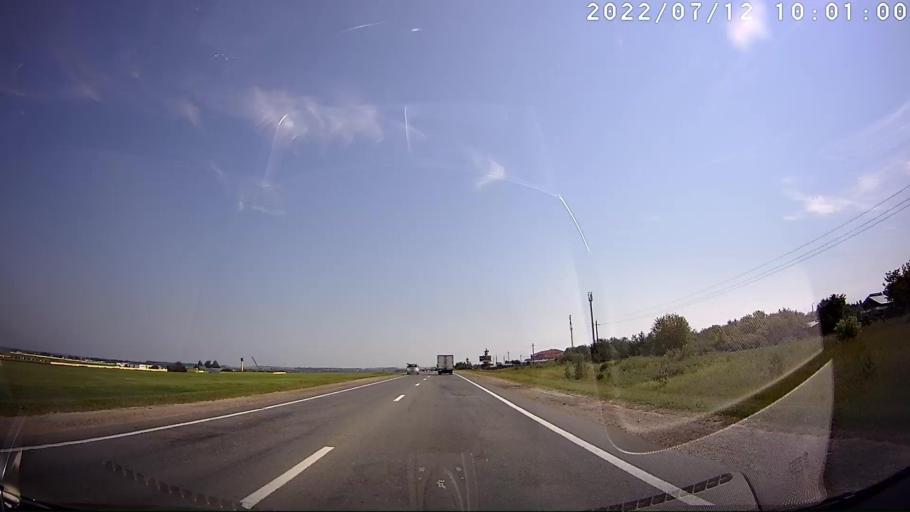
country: RU
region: Mariy-El
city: Yoshkar-Ola
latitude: 56.6649
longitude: 47.9883
